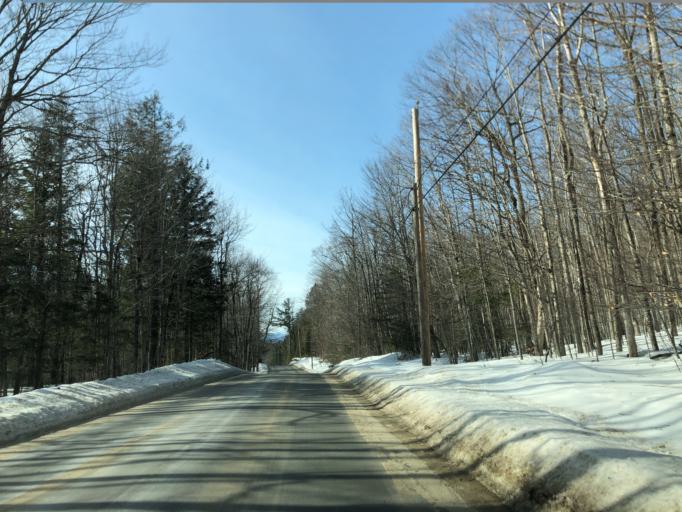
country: US
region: Maine
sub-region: Oxford County
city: Paris
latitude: 44.2672
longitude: -70.4761
